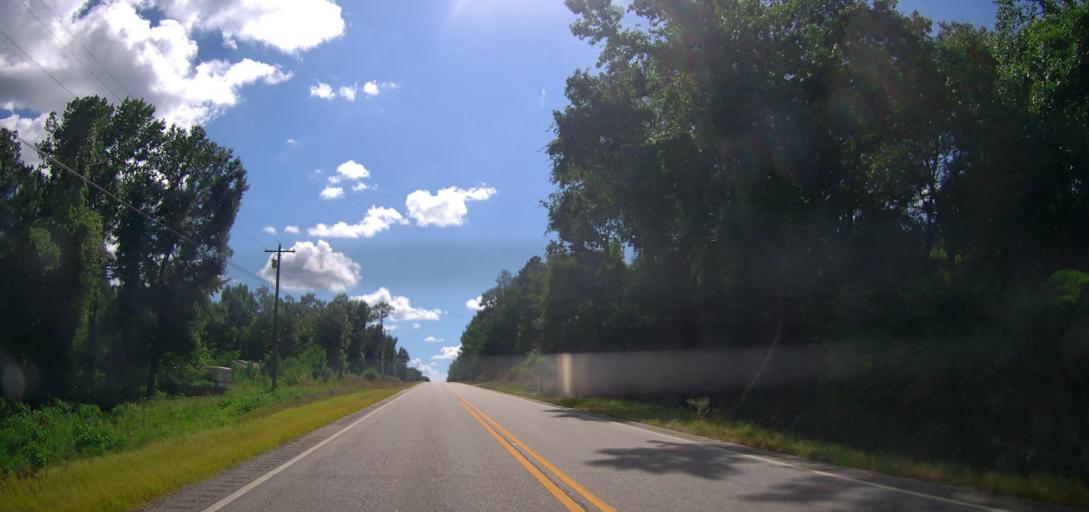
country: US
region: Alabama
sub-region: Macon County
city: Tuskegee
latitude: 32.4614
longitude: -85.6113
